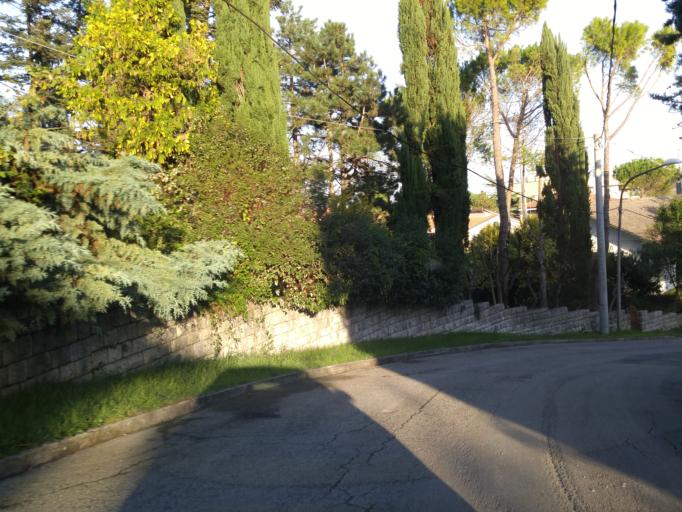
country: IT
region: The Marches
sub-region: Provincia di Pesaro e Urbino
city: Calcinelli
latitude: 43.7505
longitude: 12.9152
